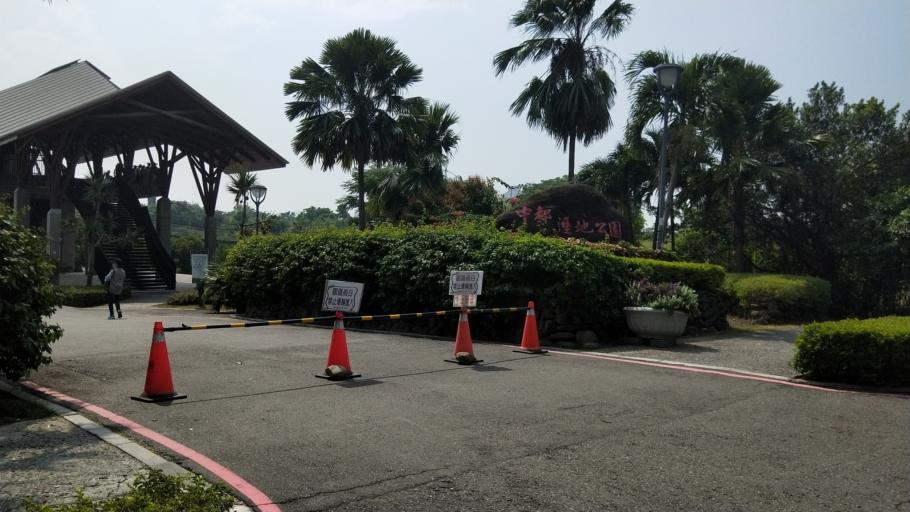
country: TW
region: Kaohsiung
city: Kaohsiung
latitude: 22.6482
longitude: 120.2853
